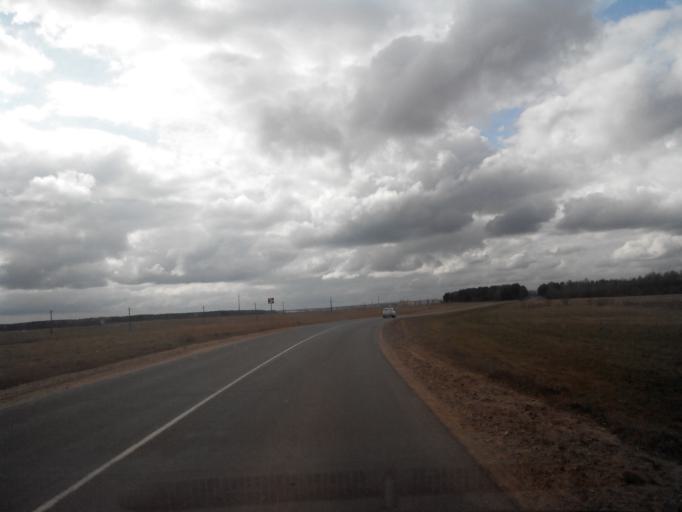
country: BY
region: Vitebsk
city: Pastavy
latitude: 55.1114
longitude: 26.9026
